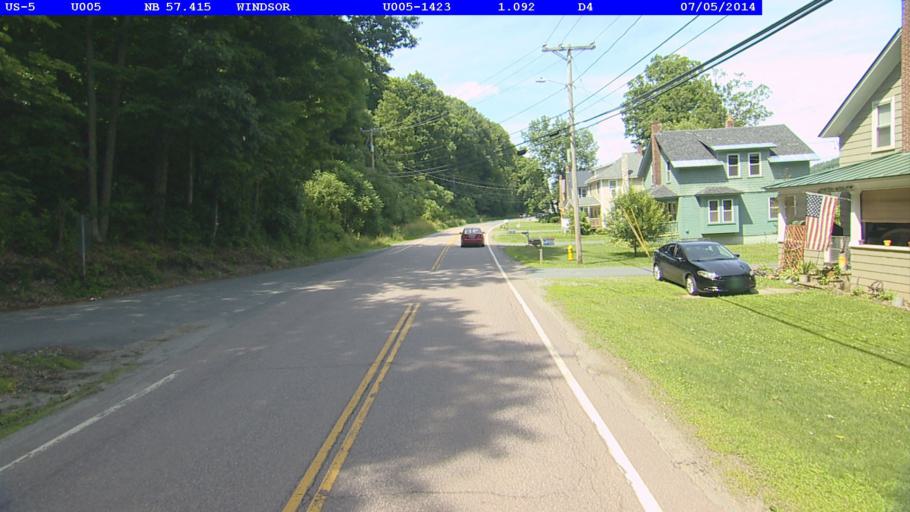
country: US
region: Vermont
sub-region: Windsor County
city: Windsor
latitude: 43.4443
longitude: -72.3982
